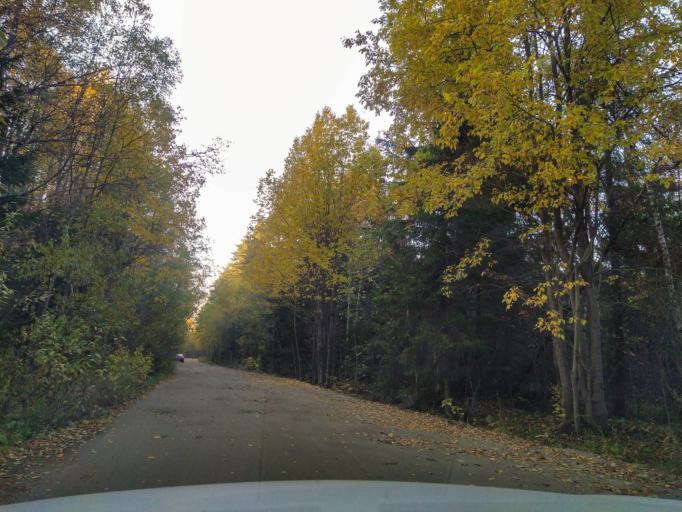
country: RU
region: Leningrad
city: Kuznechnoye
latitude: 61.3028
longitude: 30.0480
